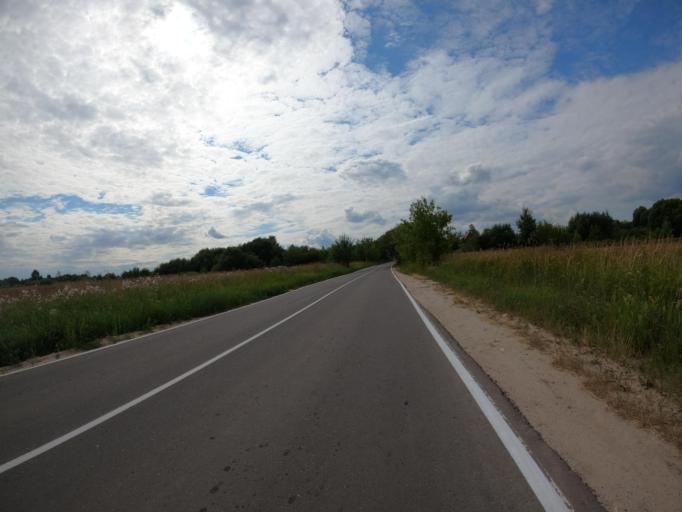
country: RU
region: Moskovskaya
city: Bronnitsy
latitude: 55.4895
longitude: 38.2405
